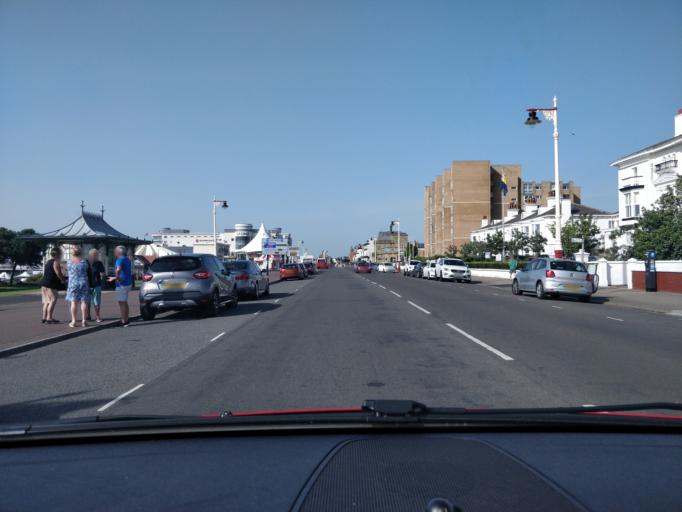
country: GB
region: England
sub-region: Sefton
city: Southport
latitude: 53.6489
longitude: -3.0089
